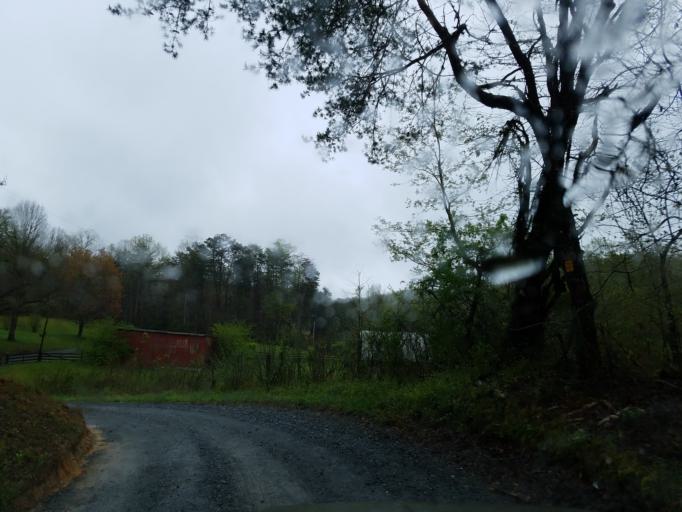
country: US
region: Georgia
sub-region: Fannin County
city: Blue Ridge
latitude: 34.8562
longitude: -84.2324
